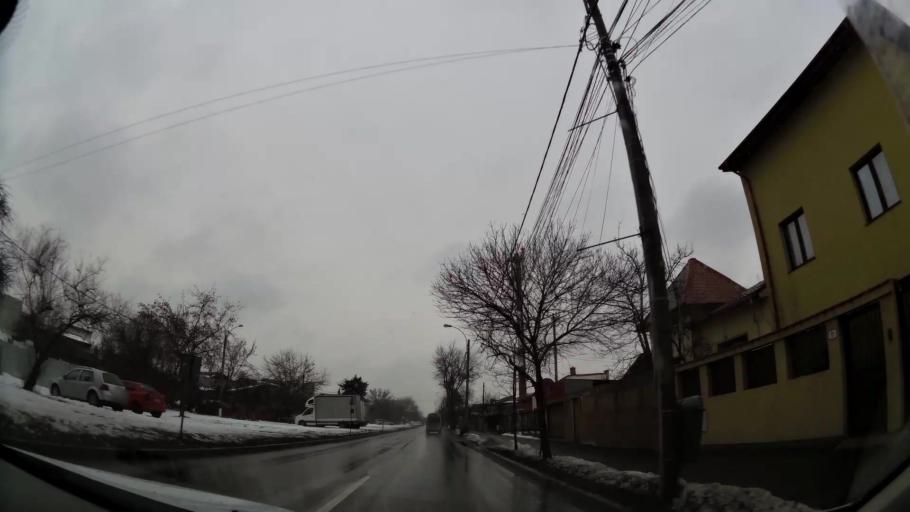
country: RO
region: Ilfov
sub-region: Comuna Mogosoaia
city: Mogosoaia
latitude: 44.4931
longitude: 26.0289
